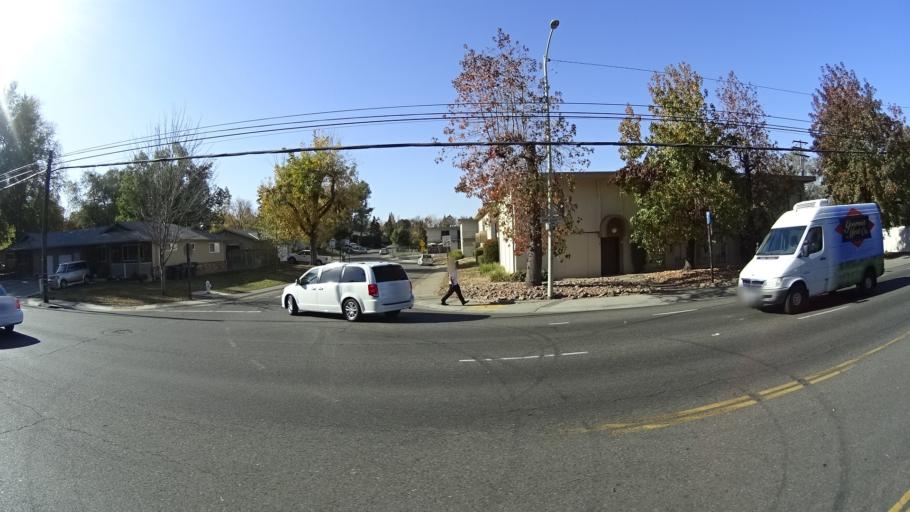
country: US
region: California
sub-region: Sacramento County
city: Fair Oaks
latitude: 38.6599
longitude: -121.2922
